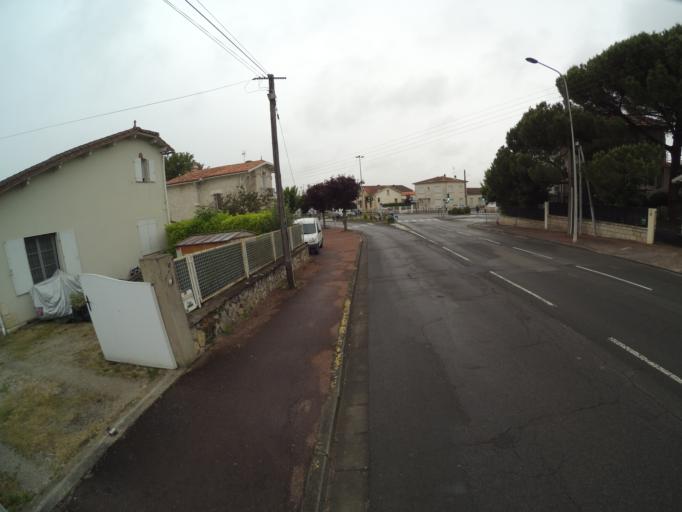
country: FR
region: Poitou-Charentes
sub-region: Departement de la Charente-Maritime
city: Royan
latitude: 45.6228
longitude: -1.0101
